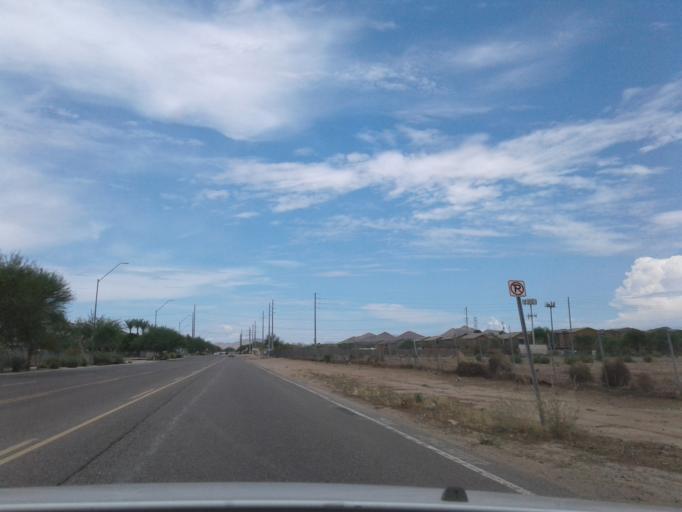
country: US
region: Arizona
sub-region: Maricopa County
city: Anthem
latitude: 33.7037
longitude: -112.1087
